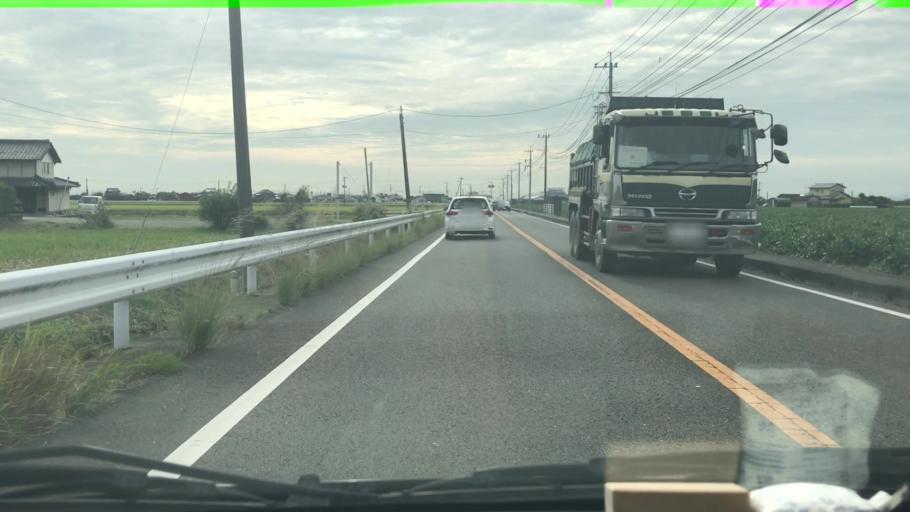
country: JP
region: Saga Prefecture
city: Takeocho-takeo
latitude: 33.2019
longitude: 130.0959
